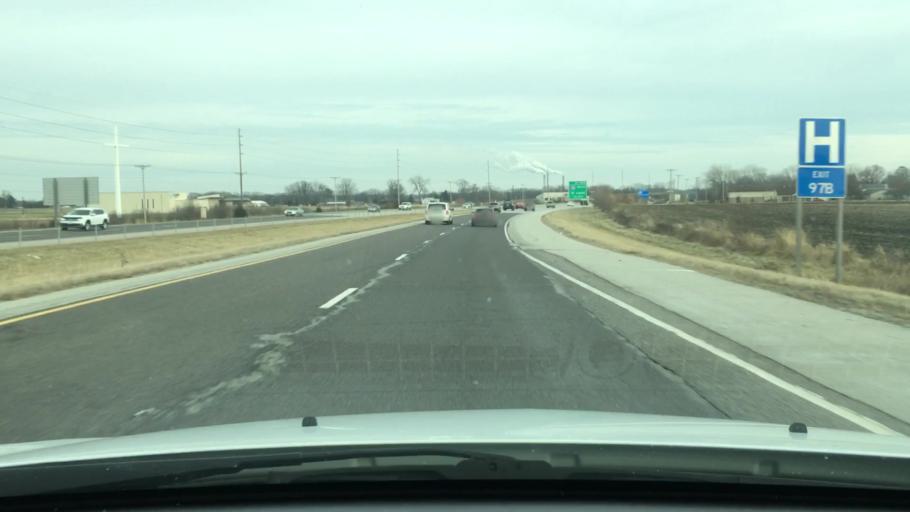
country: US
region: Illinois
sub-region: Sangamon County
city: Southern View
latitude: 39.7418
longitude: -89.6629
